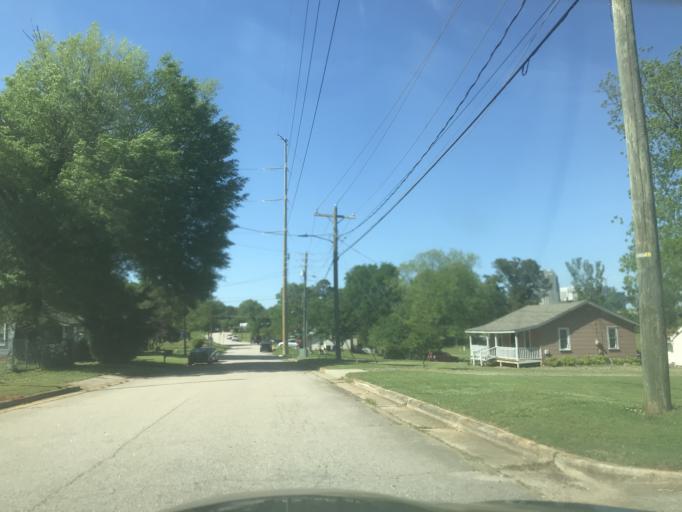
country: US
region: North Carolina
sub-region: Wake County
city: Raleigh
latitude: 35.7621
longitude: -78.6479
